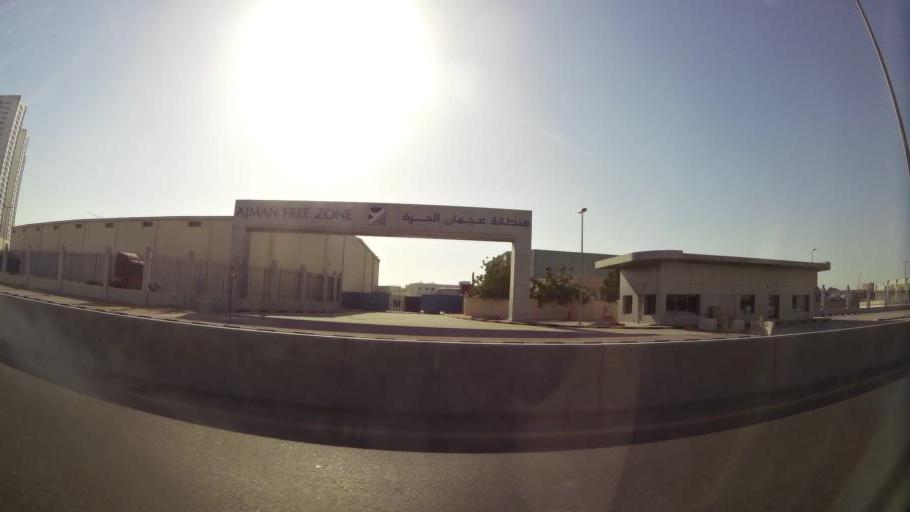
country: AE
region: Ajman
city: Ajman
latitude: 25.3952
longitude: 55.4715
